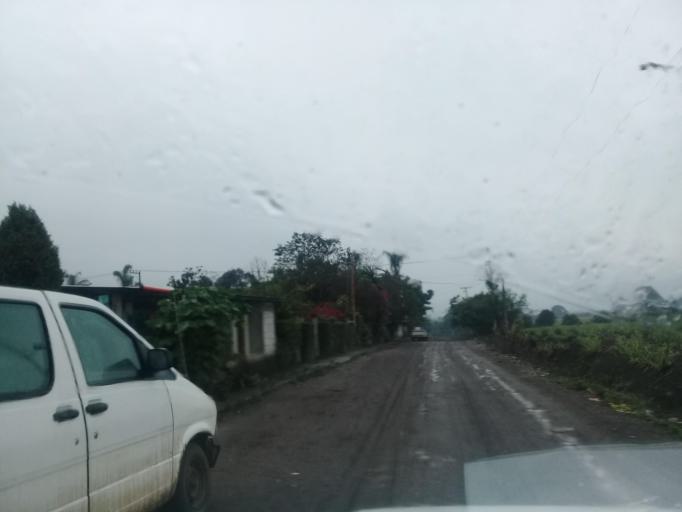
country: MX
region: Veracruz
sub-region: Cordoba
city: San Jose de Tapia
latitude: 18.8470
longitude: -96.9571
